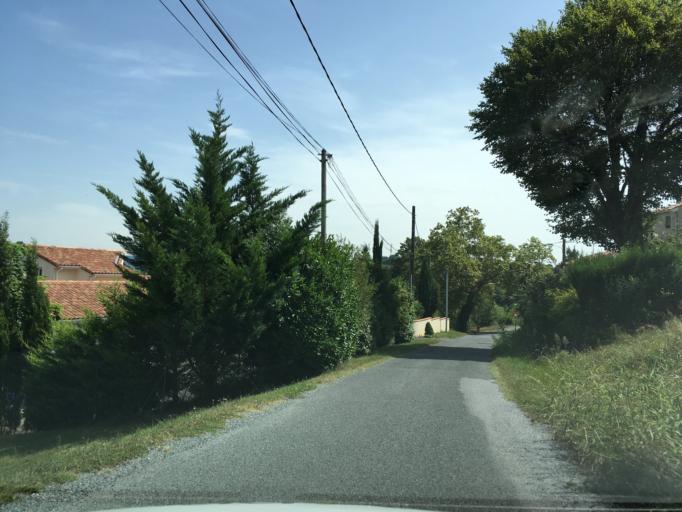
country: FR
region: Midi-Pyrenees
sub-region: Departement du Tarn
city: Castres
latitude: 43.6356
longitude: 2.2285
